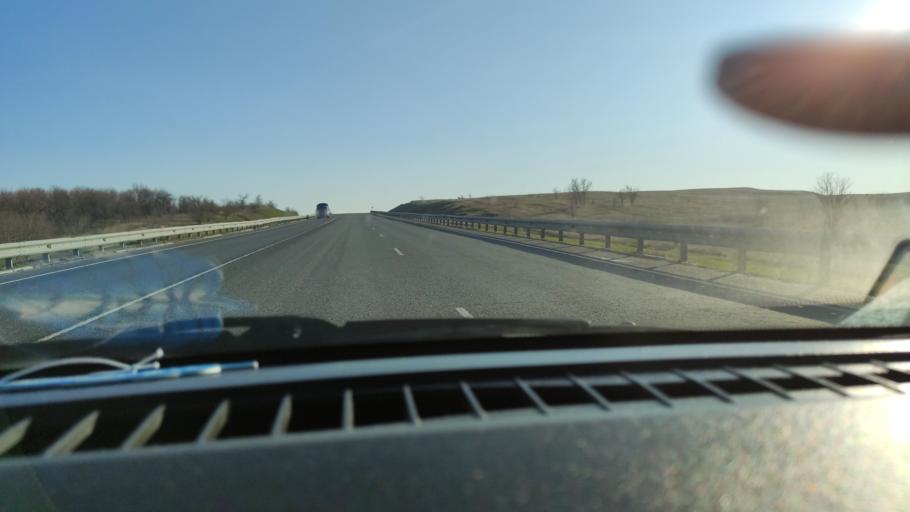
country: RU
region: Saratov
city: Alekseyevka
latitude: 52.2194
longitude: 47.8949
